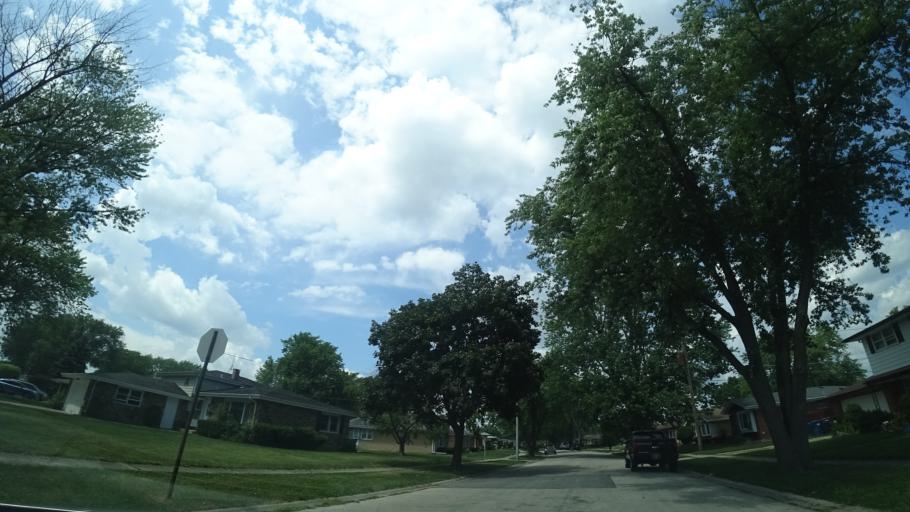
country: US
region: Illinois
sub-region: Cook County
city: Alsip
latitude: 41.6772
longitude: -87.7269
